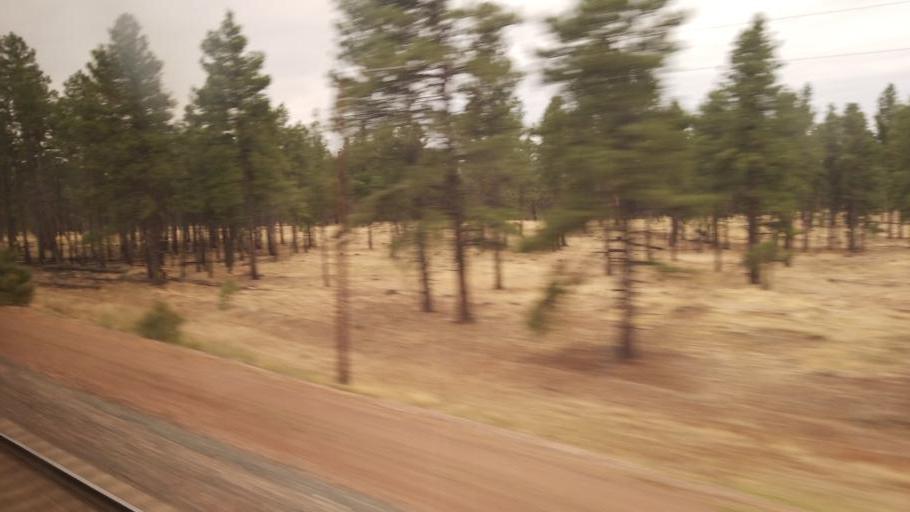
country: US
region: Arizona
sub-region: Coconino County
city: Parks
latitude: 35.2461
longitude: -112.0539
